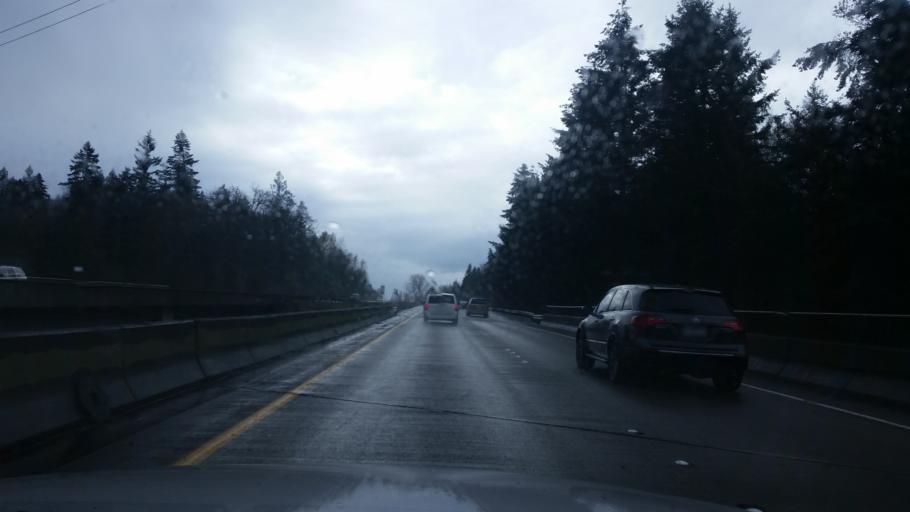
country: US
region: Washington
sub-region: King County
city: Covington
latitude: 47.3483
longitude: -122.1384
